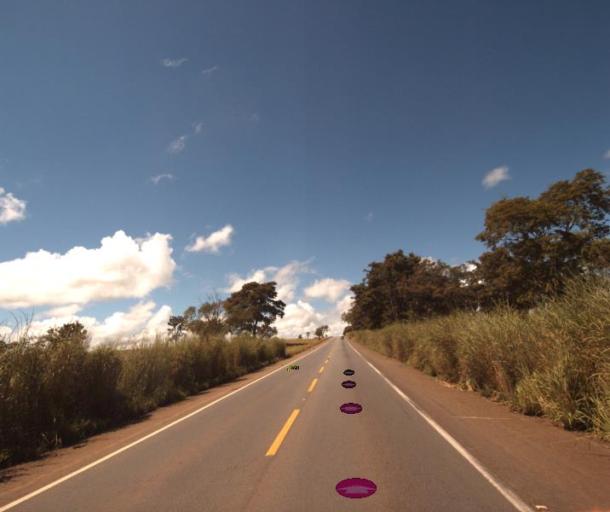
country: BR
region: Goias
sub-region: Jaragua
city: Jaragua
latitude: -15.8230
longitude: -49.2846
